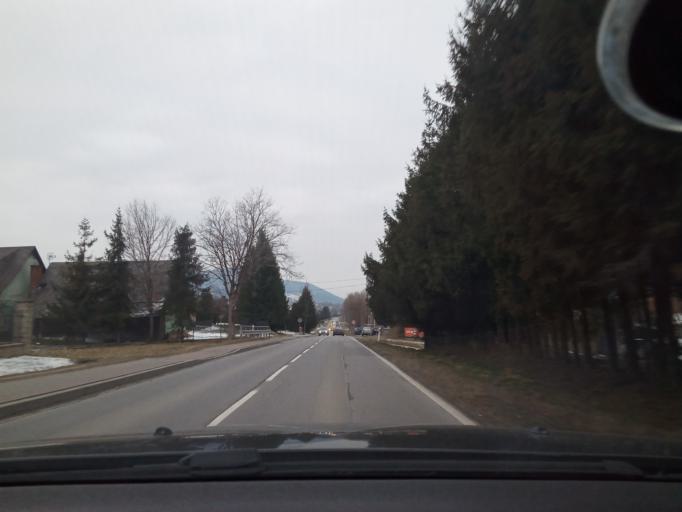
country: PL
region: Lesser Poland Voivodeship
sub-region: Powiat limanowski
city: Mszana Gorna
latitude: 49.6592
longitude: 20.1021
